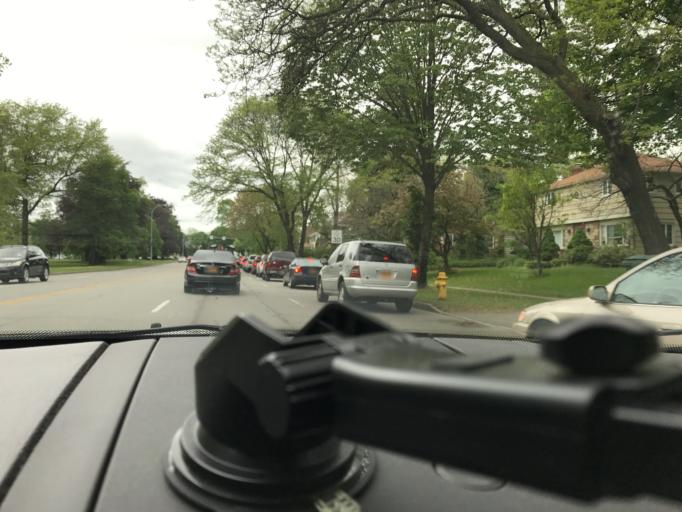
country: US
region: New York
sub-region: Monroe County
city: Rochester
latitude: 43.1251
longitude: -77.6360
